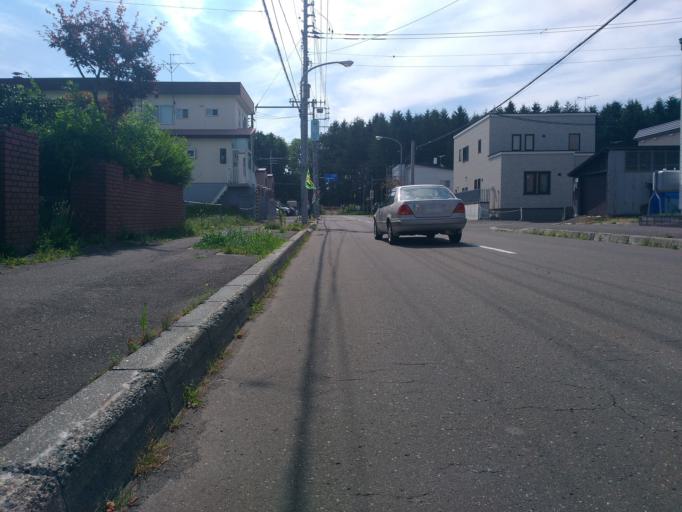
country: JP
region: Hokkaido
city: Ebetsu
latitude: 43.0757
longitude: 141.5014
